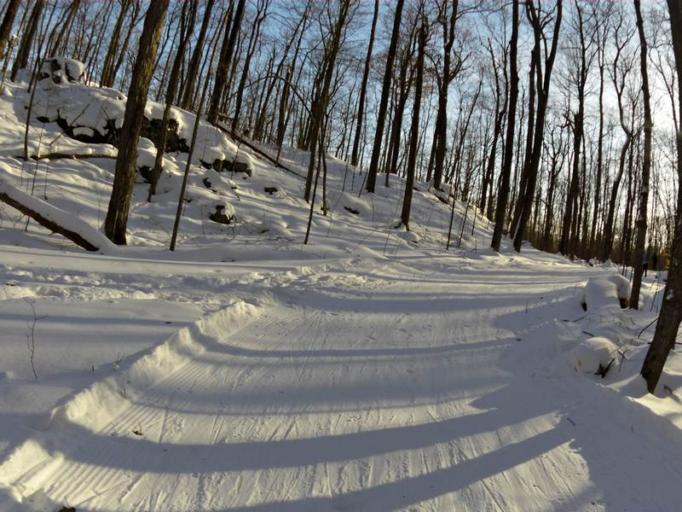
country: CA
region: Quebec
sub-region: Outaouais
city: Gatineau
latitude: 45.4751
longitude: -75.7949
